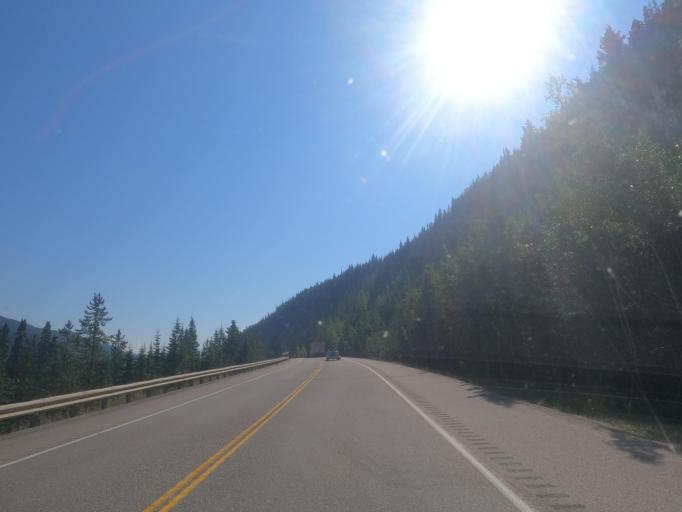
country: CA
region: Alberta
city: Jasper Park Lodge
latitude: 52.8774
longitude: -118.3423
